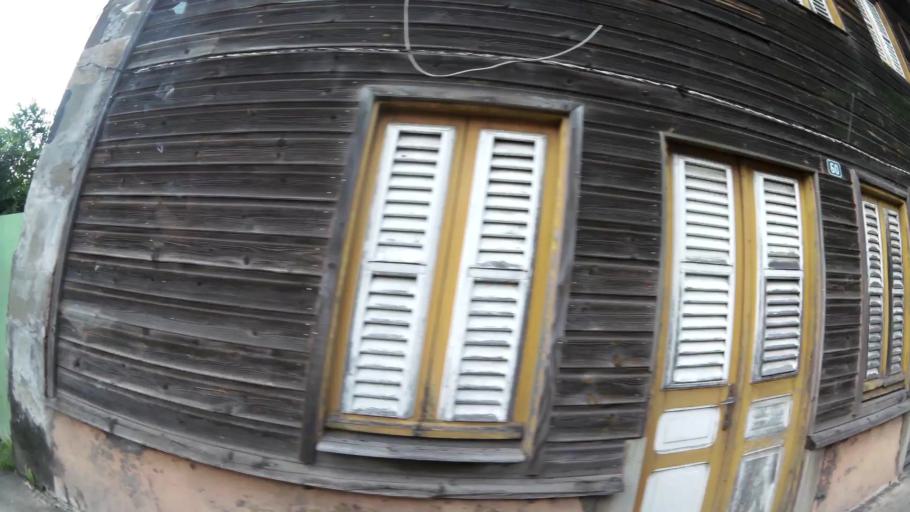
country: MQ
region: Martinique
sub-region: Martinique
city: Saint-Pierre
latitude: 14.7063
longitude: -61.1832
